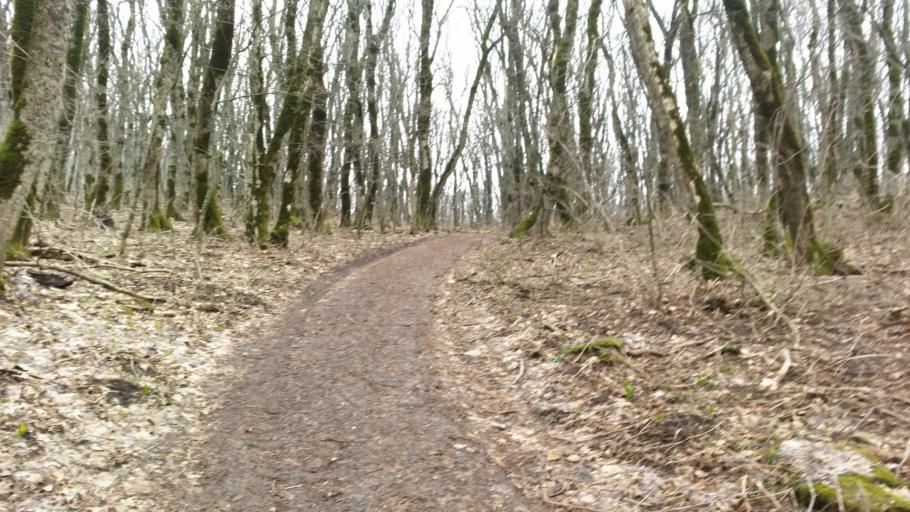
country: RU
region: Stavropol'skiy
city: Zheleznovodsk
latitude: 44.1555
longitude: 43.0430
